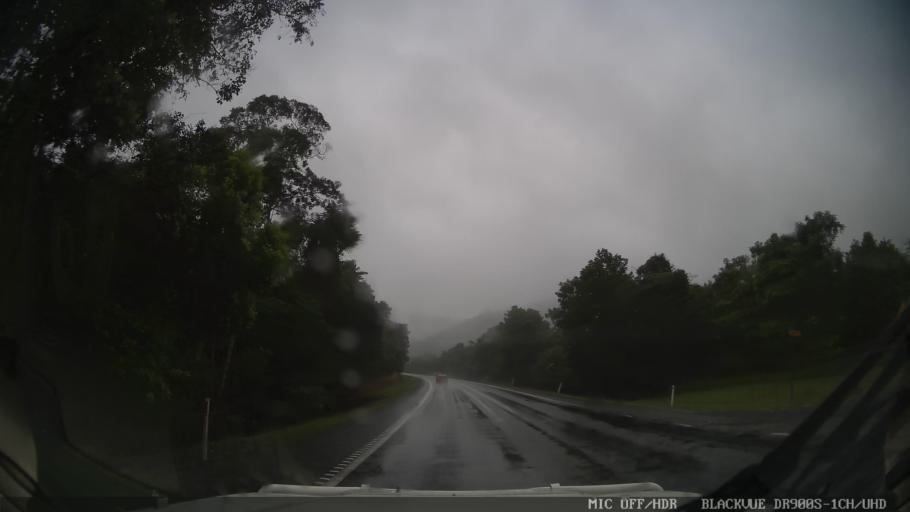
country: AU
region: Queensland
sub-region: Cassowary Coast
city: Innisfail
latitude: -17.8633
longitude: 145.9846
